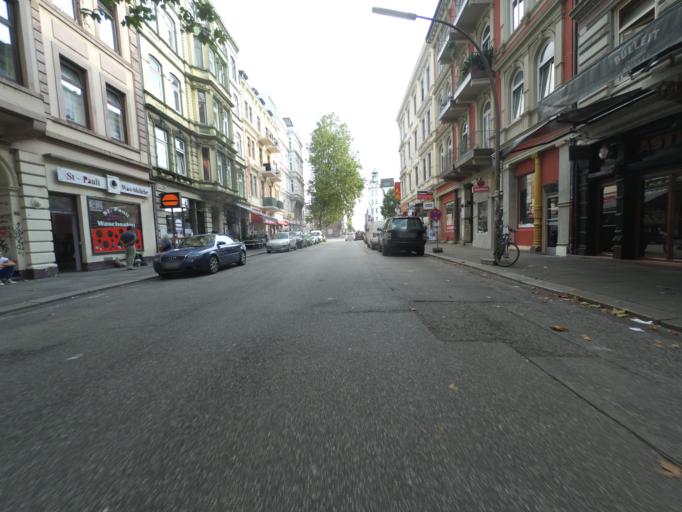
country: DE
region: Hamburg
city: St. Pauli
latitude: 53.5503
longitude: 9.9621
